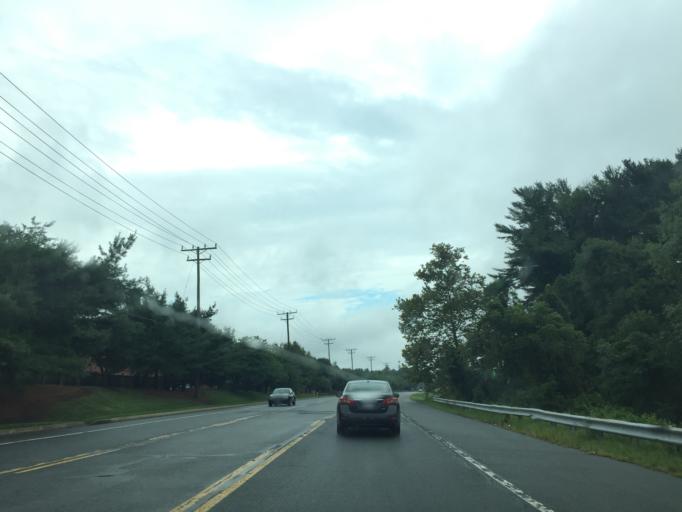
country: US
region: Maryland
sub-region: Harford County
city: Bel Air South
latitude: 39.4940
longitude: -76.3234
